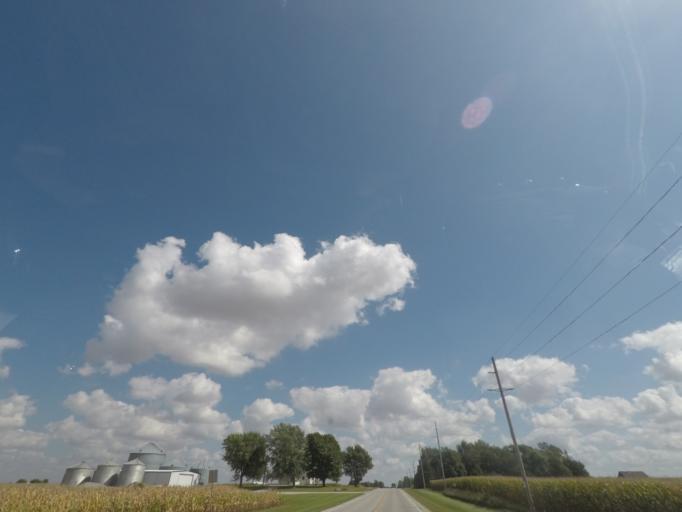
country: US
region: Iowa
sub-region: Story County
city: Nevada
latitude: 42.0227
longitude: -93.4298
